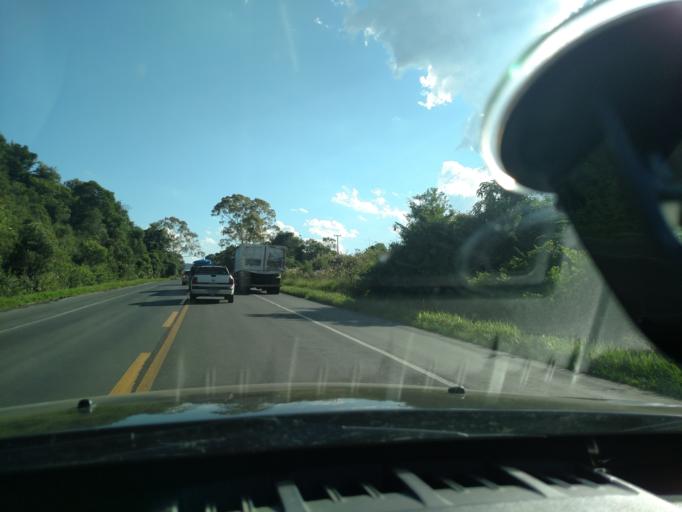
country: BR
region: Santa Catarina
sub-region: Otacilio Costa
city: Otacilio Costa
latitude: -27.2637
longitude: -50.0578
